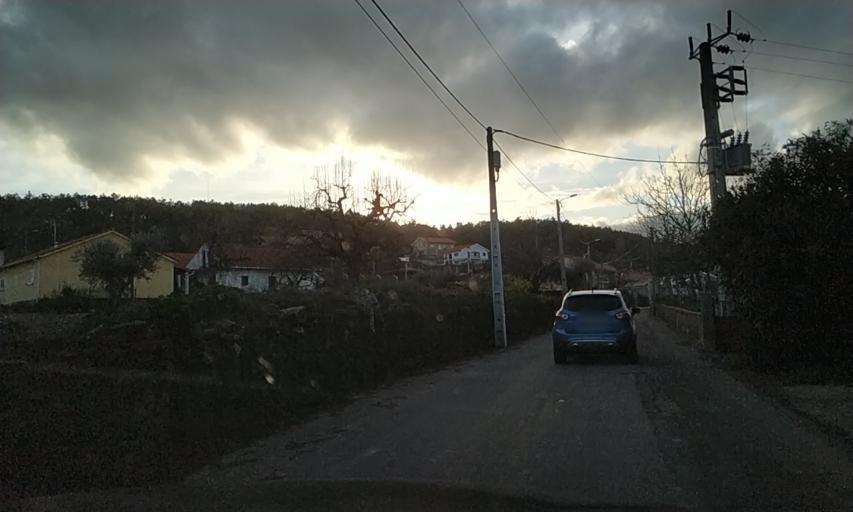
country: PT
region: Braganca
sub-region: Carrazeda de Ansiaes
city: Carrazeda de Anciaes
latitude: 41.2199
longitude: -7.3460
